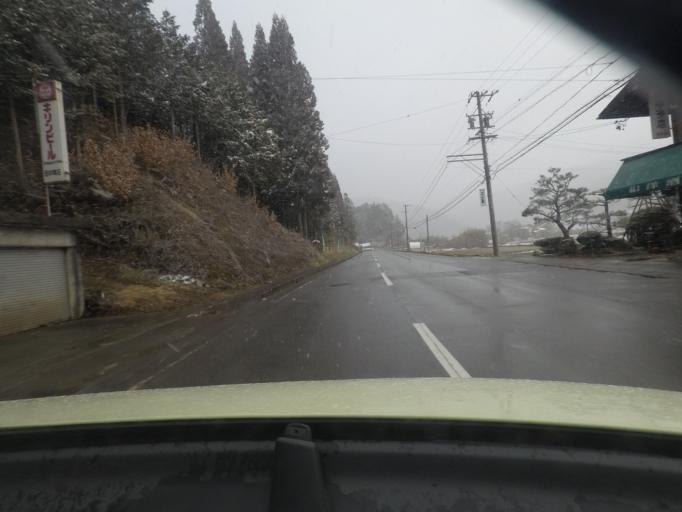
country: JP
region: Gifu
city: Takayama
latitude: 36.1417
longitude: 137.3096
